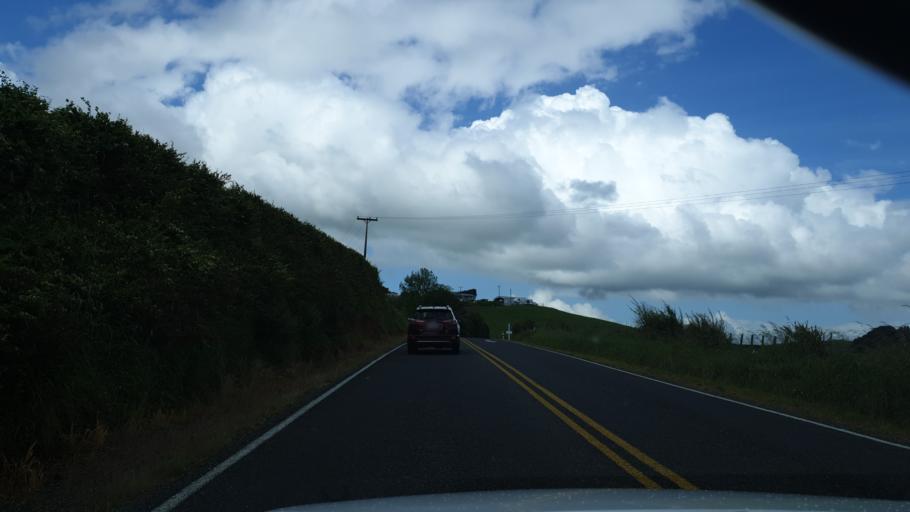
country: NZ
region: Waikato
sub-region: Matamata-Piako District
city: Matamata
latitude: -37.8789
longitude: 175.6983
